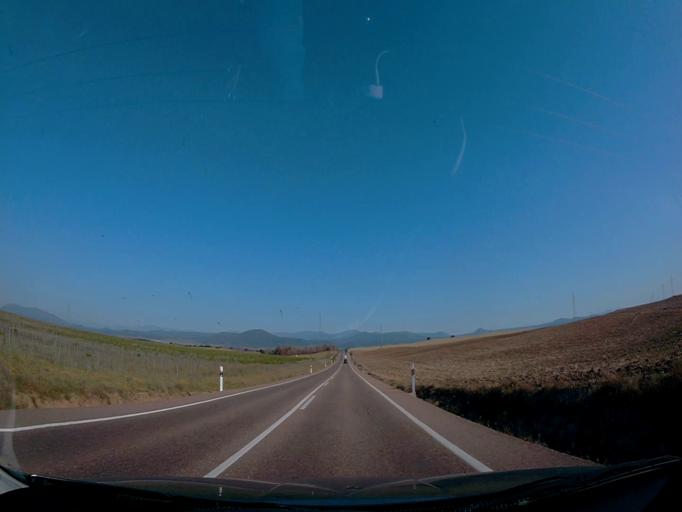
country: ES
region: Castille-La Mancha
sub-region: Province of Toledo
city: Hormigos
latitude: 40.1089
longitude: -4.3999
